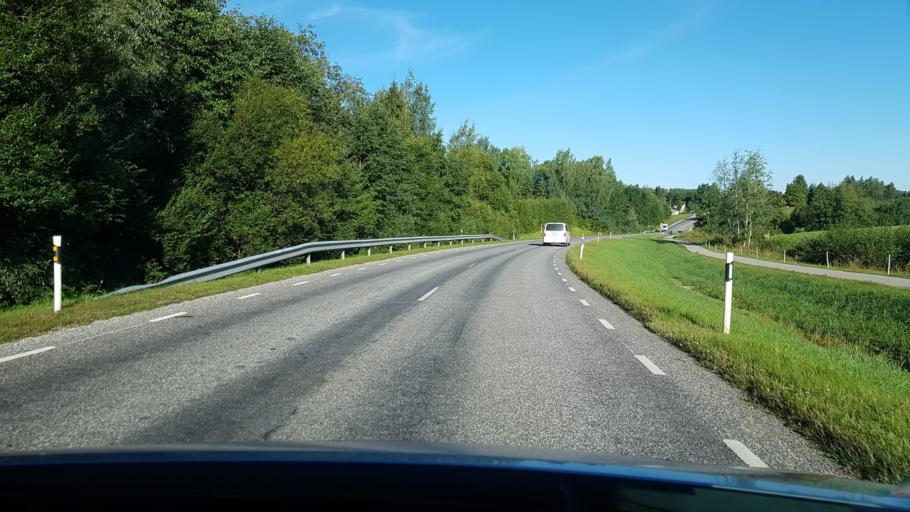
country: EE
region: Vorumaa
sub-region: Antsla vald
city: Vana-Antsla
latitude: 58.0496
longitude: 26.5414
